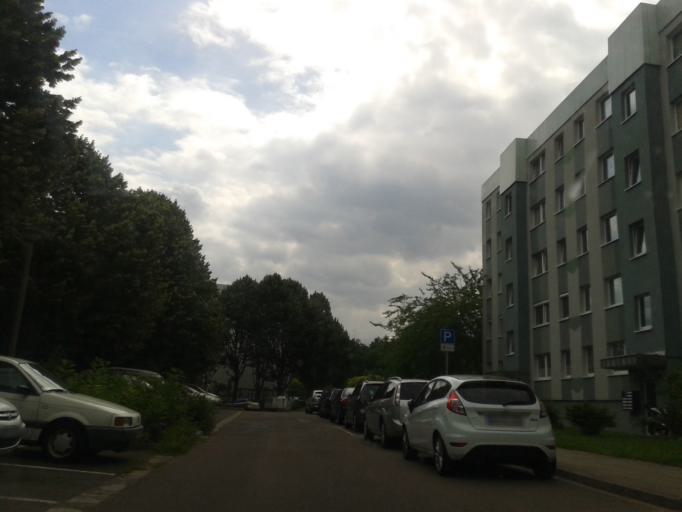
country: DE
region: Saxony
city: Dresden
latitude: 51.0114
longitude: 13.7755
